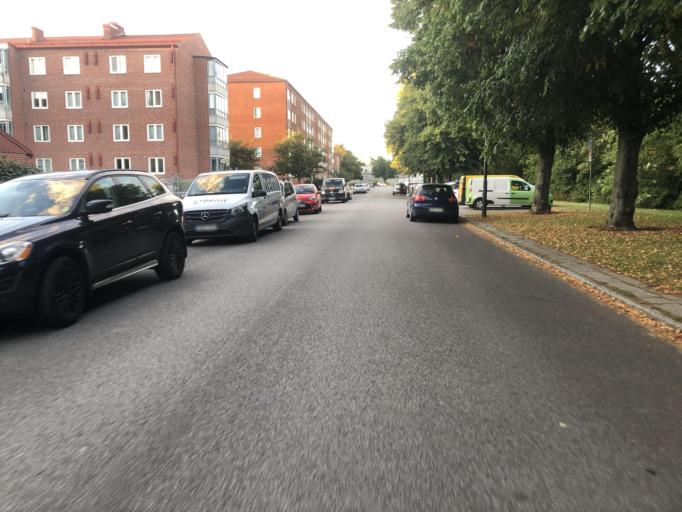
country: SE
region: Skane
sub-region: Malmo
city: Malmoe
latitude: 55.5922
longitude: 13.0319
